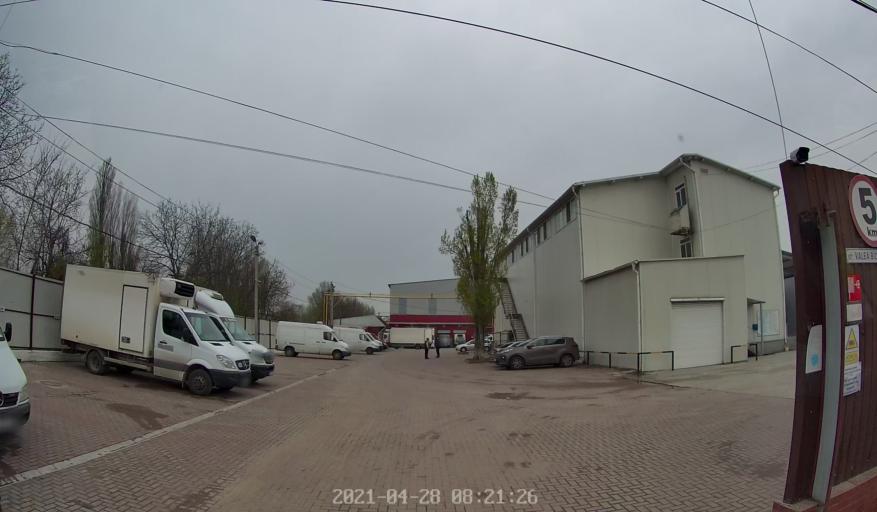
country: MD
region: Chisinau
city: Chisinau
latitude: 46.9891
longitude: 28.8923
